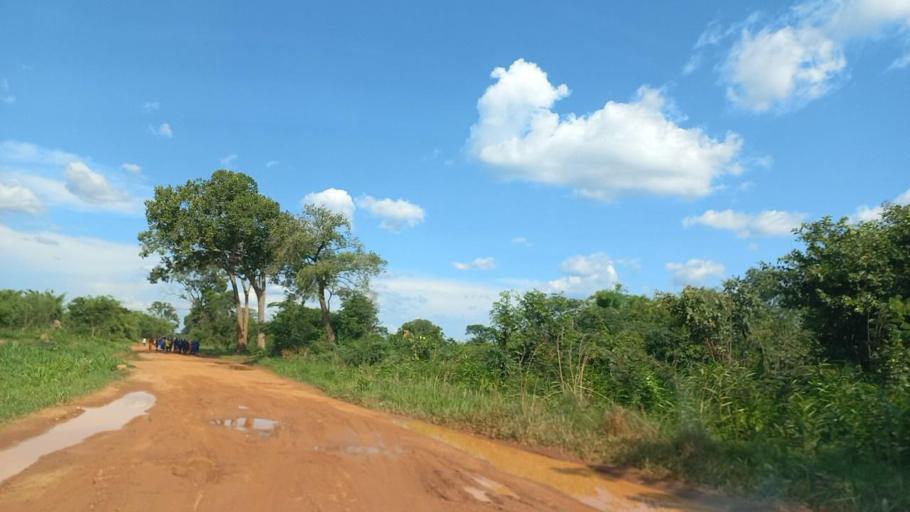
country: ZM
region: Copperbelt
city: Kitwe
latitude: -12.8645
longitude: 28.3753
